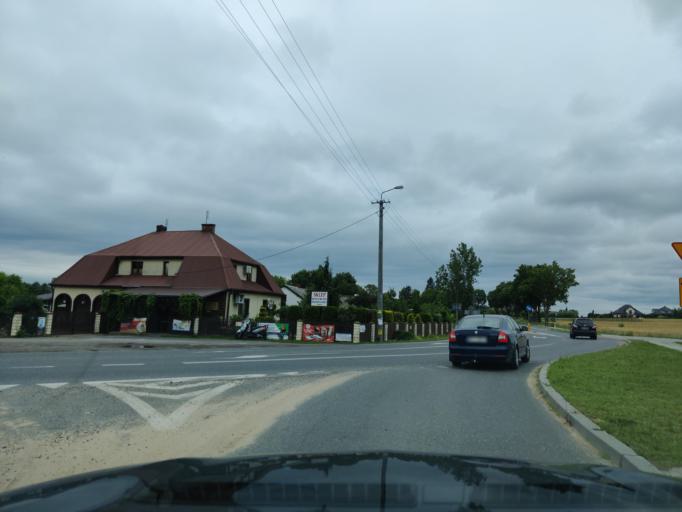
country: PL
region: Masovian Voivodeship
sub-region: Powiat pultuski
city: Pultusk
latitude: 52.7591
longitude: 21.0672
